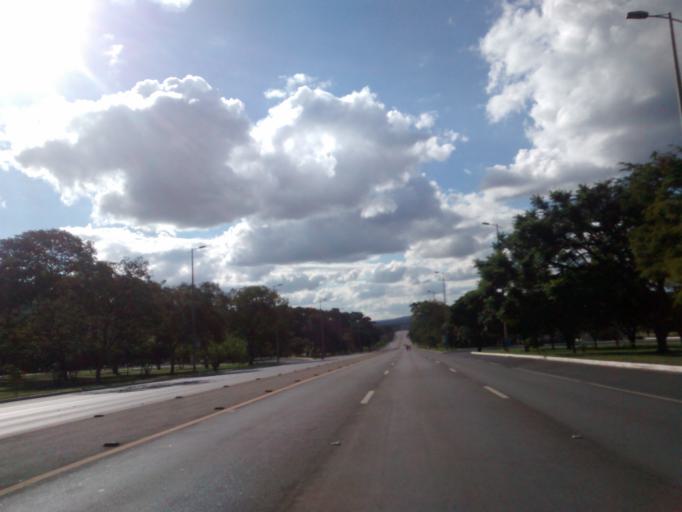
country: BR
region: Federal District
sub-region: Brasilia
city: Brasilia
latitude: -15.7576
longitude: -47.8855
